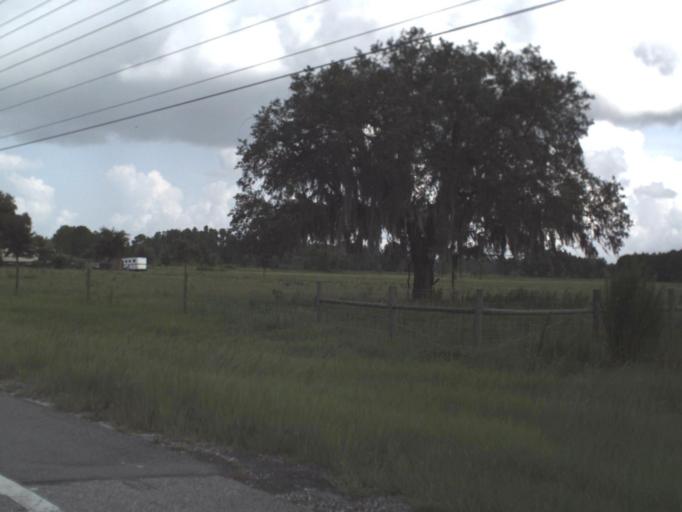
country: US
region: Florida
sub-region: Pasco County
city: Land O' Lakes
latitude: 28.3218
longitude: -82.4444
